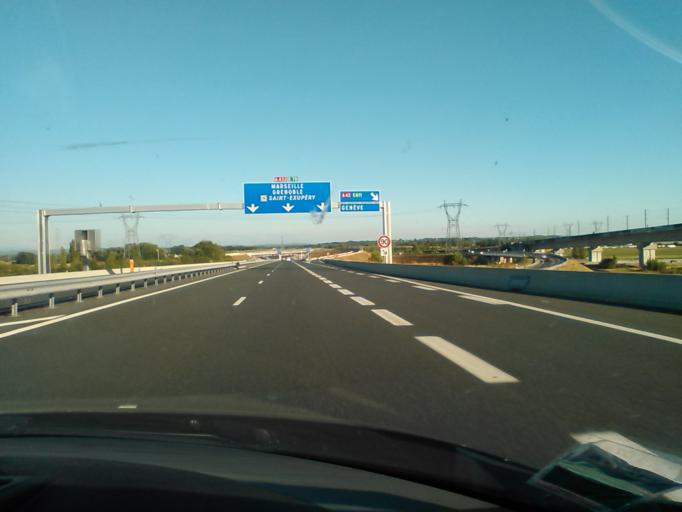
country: FR
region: Rhone-Alpes
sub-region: Departement de l'Ain
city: La Boisse
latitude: 45.8341
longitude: 5.0237
